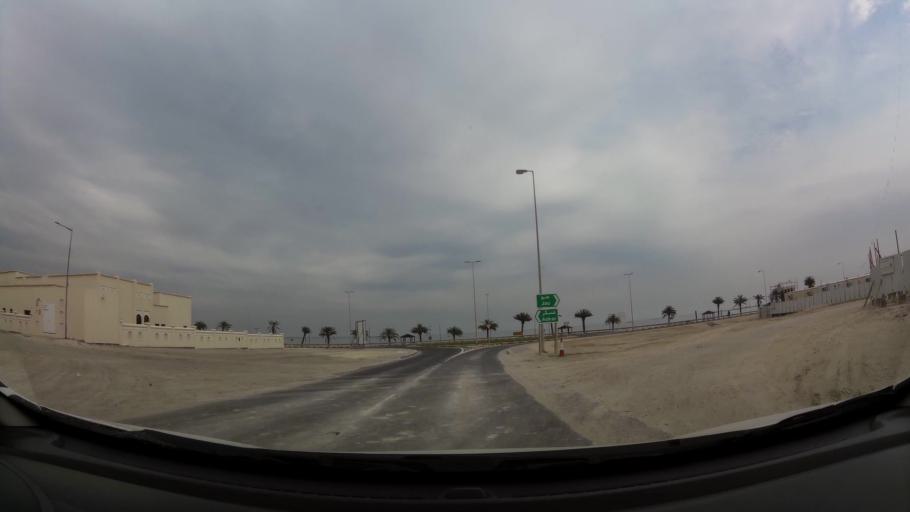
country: BH
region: Northern
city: Ar Rifa'
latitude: 26.0482
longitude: 50.6191
